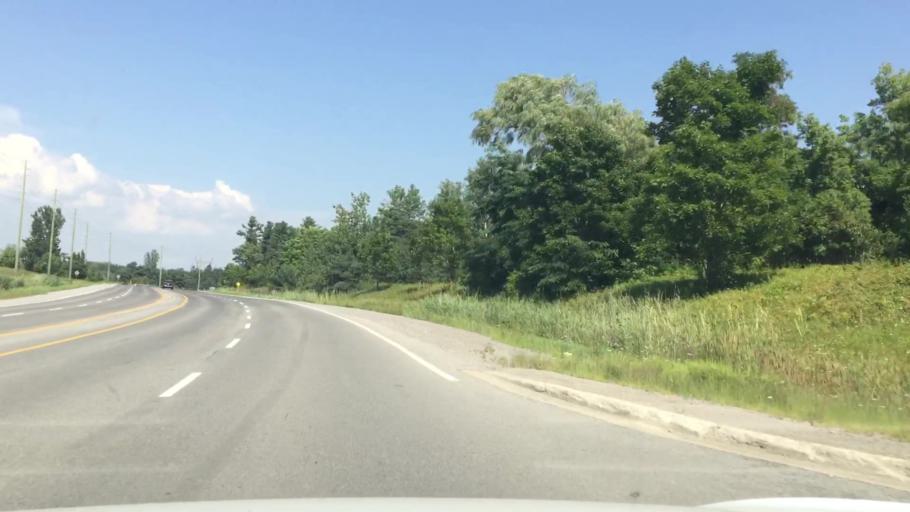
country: CA
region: Ontario
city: Pickering
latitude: 43.8827
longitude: -79.0977
